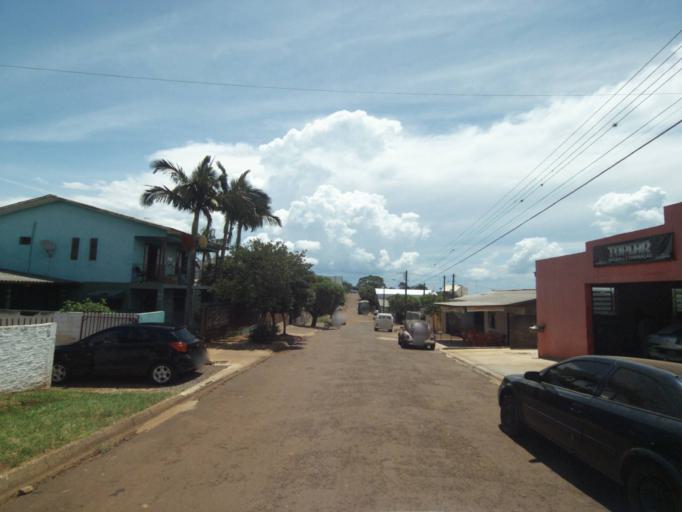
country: BR
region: Parana
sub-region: Guaraniacu
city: Guaraniacu
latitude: -25.0959
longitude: -52.8745
